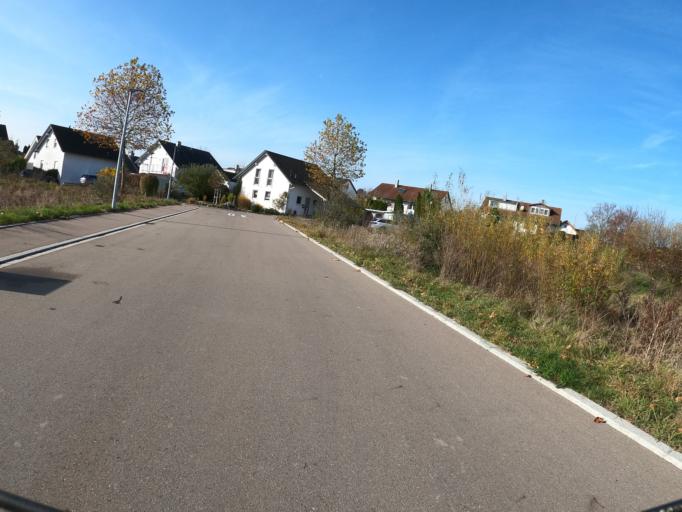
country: DE
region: Bavaria
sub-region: Swabia
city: Nersingen
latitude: 48.4572
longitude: 10.1111
